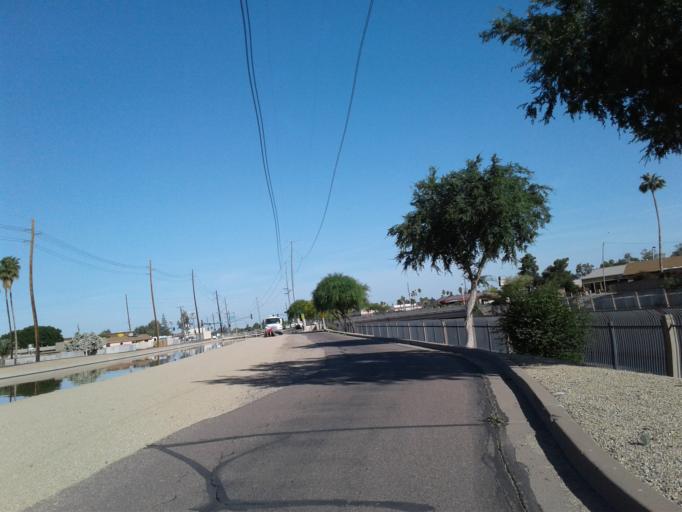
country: US
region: Arizona
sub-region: Maricopa County
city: Glendale
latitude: 33.5806
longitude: -112.1490
